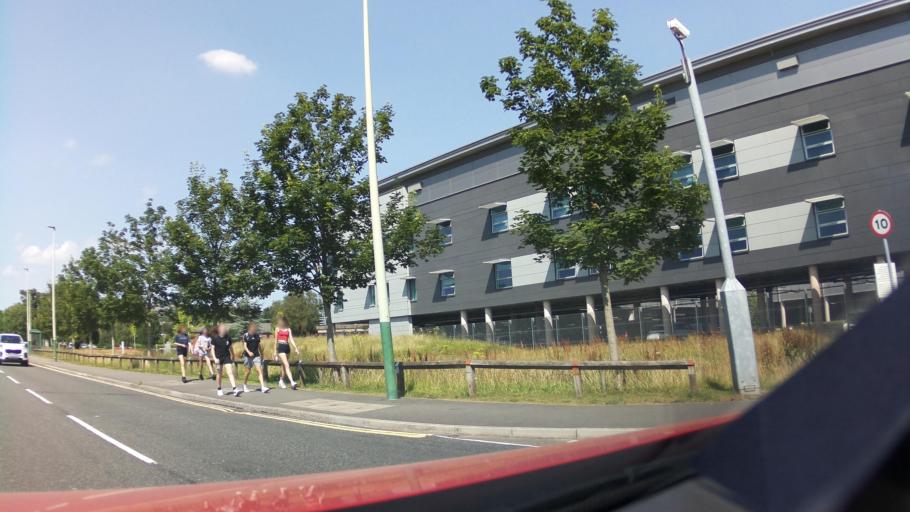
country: GB
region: Wales
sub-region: Caerphilly County Borough
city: Maesycwmmer
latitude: 51.6348
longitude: -3.2359
